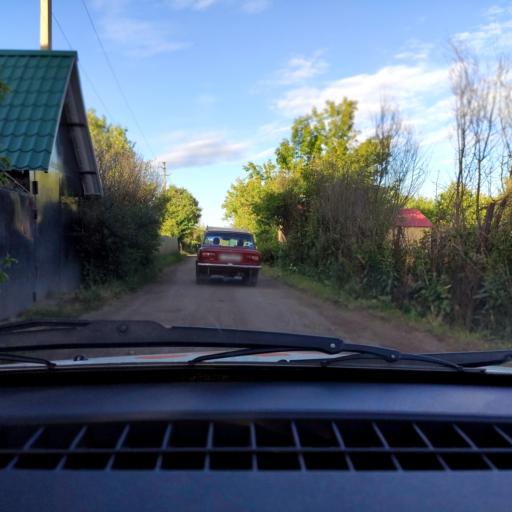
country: RU
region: Bashkortostan
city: Mikhaylovka
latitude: 54.9264
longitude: 55.7527
